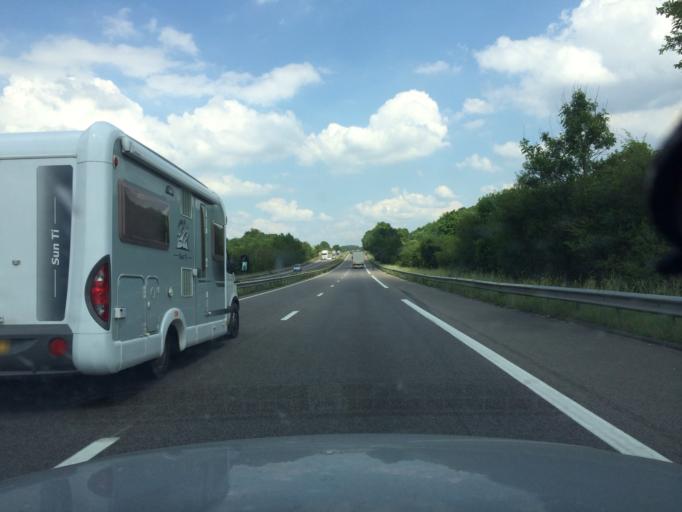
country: FR
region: Lorraine
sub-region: Departement de Meurthe-et-Moselle
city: Laxou
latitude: 48.6937
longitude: 6.0873
